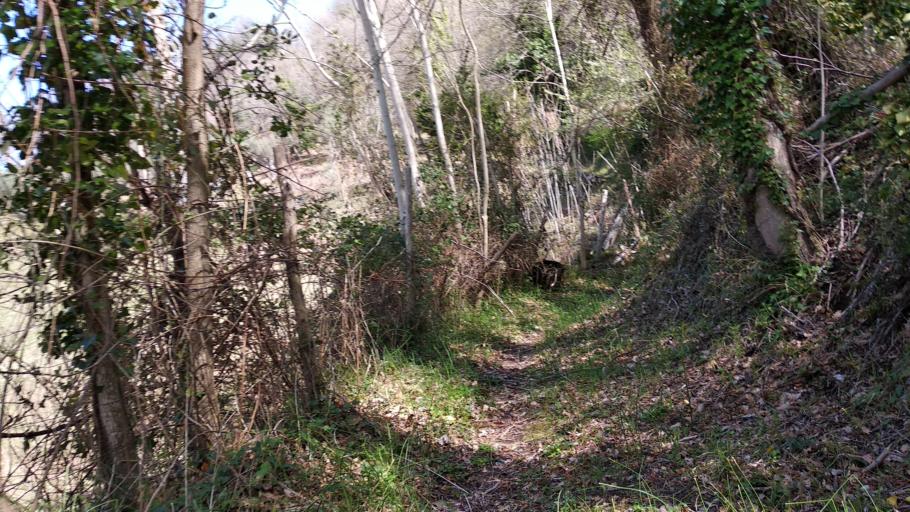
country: IT
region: Calabria
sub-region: Provincia di Cosenza
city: Altilia
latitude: 39.1277
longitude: 16.2488
